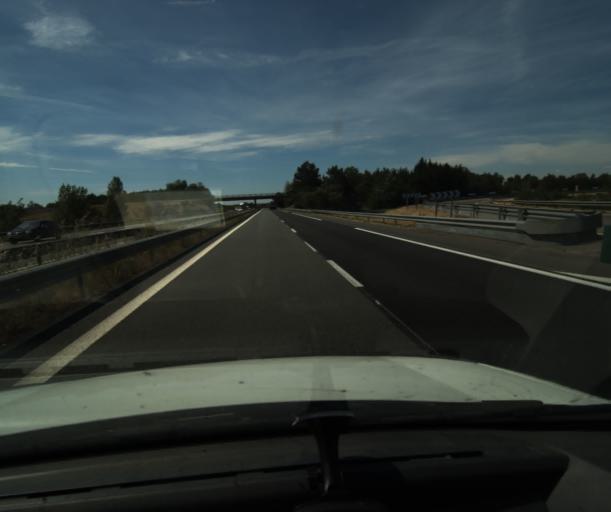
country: FR
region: Midi-Pyrenees
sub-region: Departement du Tarn-et-Garonne
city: Campsas
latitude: 43.9263
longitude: 1.3112
